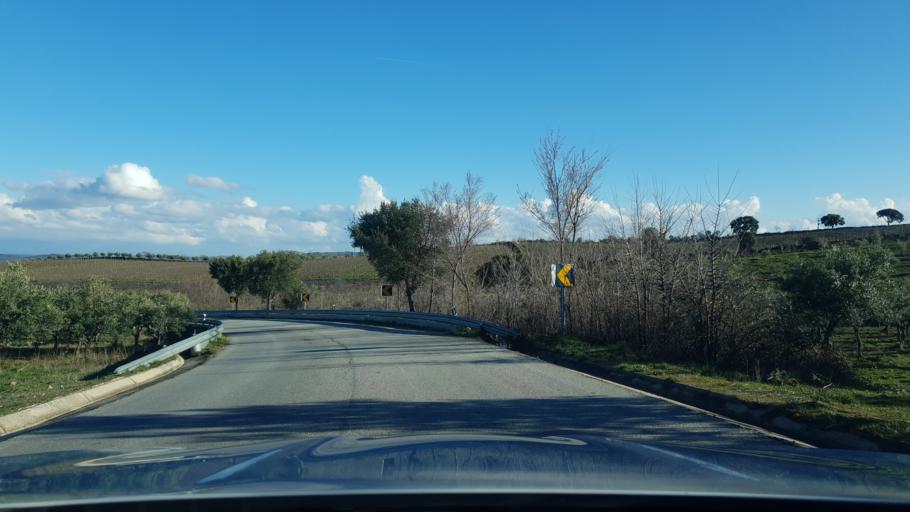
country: PT
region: Braganca
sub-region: Freixo de Espada A Cinta
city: Freixo de Espada a Cinta
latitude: 41.0941
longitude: -6.8316
